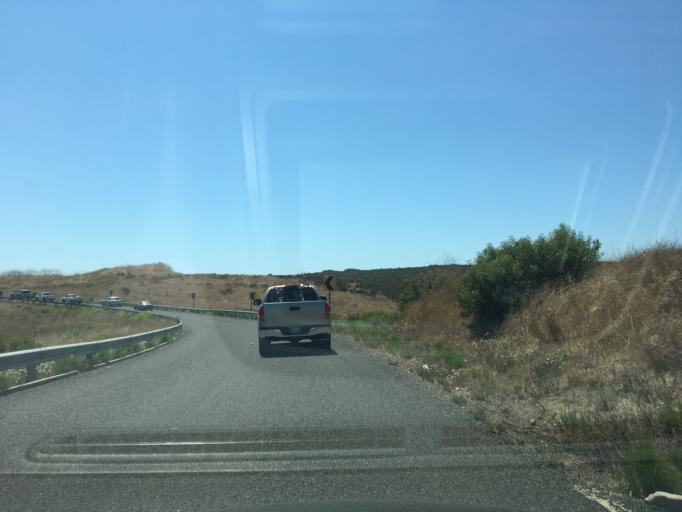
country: MX
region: Baja California
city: El Sauzal
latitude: 31.9933
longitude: -116.6973
